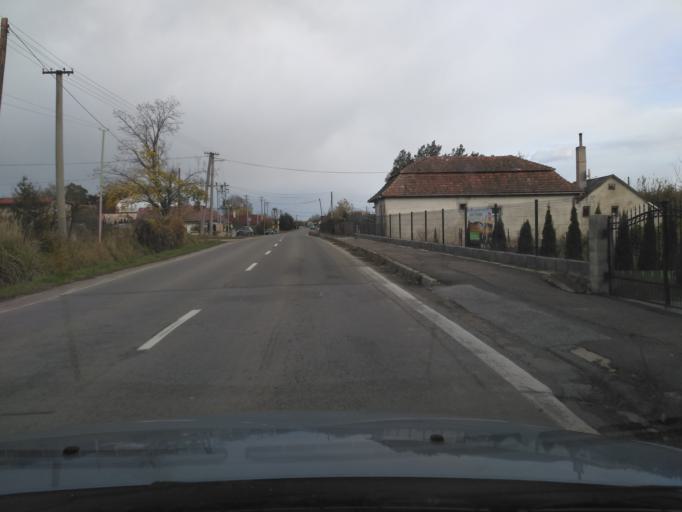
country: HU
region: Borsod-Abauj-Zemplen
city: Satoraljaujhely
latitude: 48.3981
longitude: 21.7375
